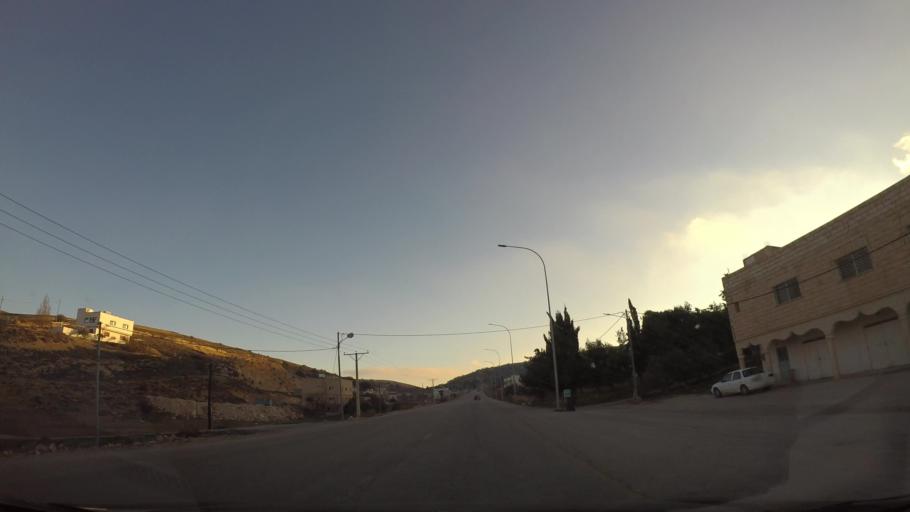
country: JO
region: Ma'an
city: Petra
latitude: 30.4208
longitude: 35.5114
